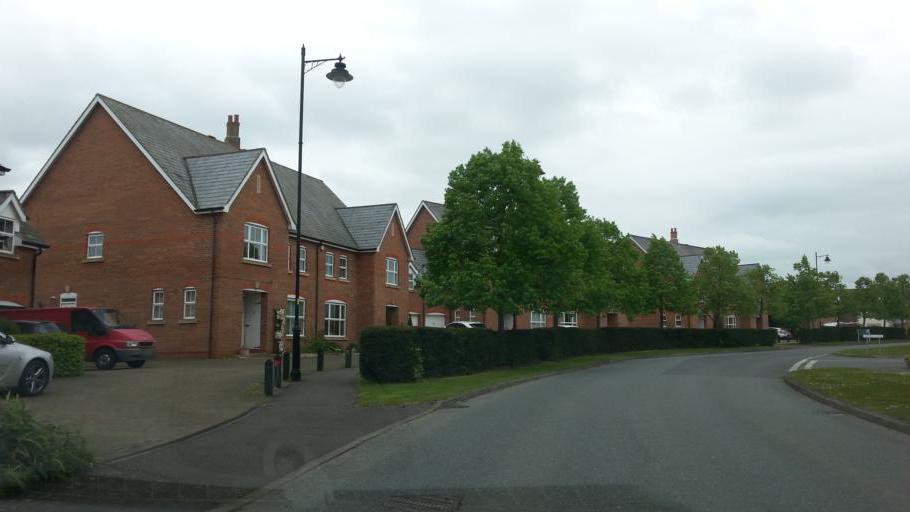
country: GB
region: England
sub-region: Lincolnshire
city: Bourne
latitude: 52.7563
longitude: -0.3709
